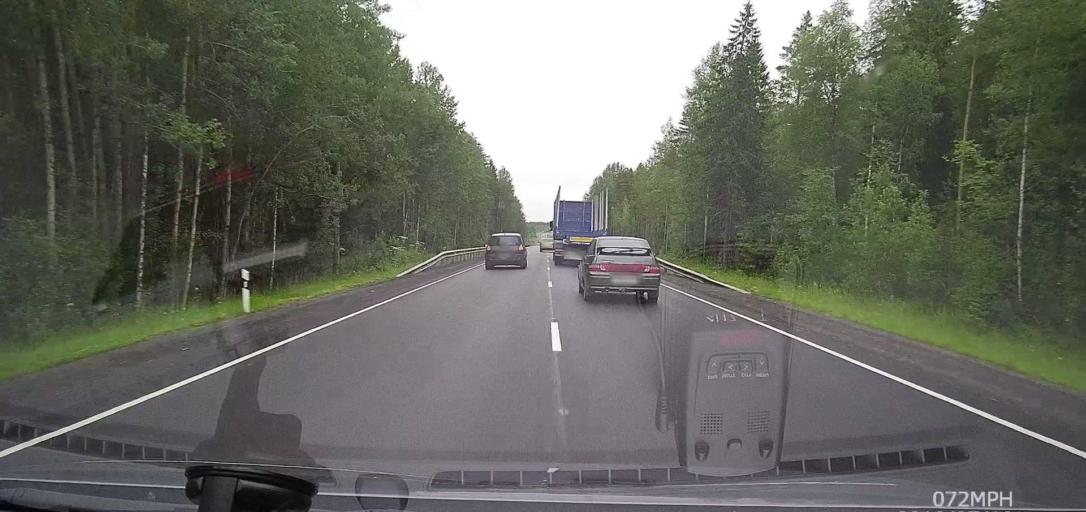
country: RU
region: Leningrad
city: Syas'stroy
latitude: 60.2633
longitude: 32.7786
